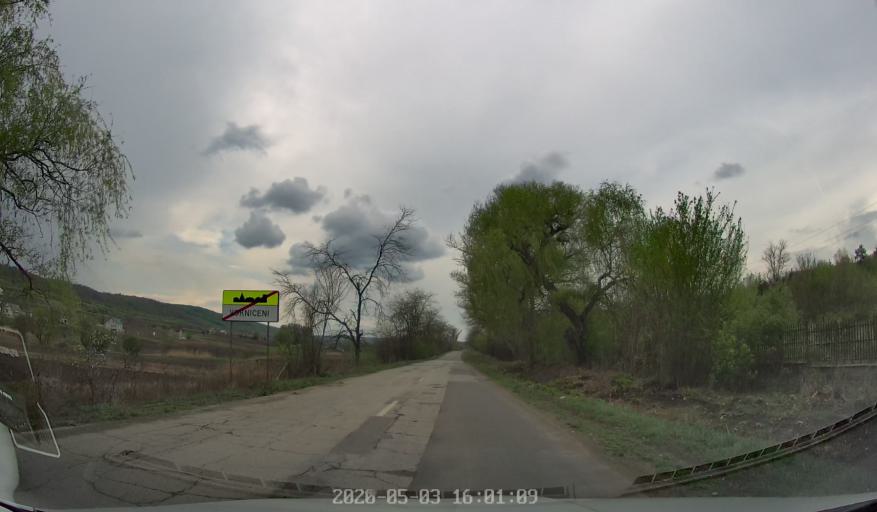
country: MD
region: Stinga Nistrului
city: Bucovat
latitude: 47.1639
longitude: 28.4125
